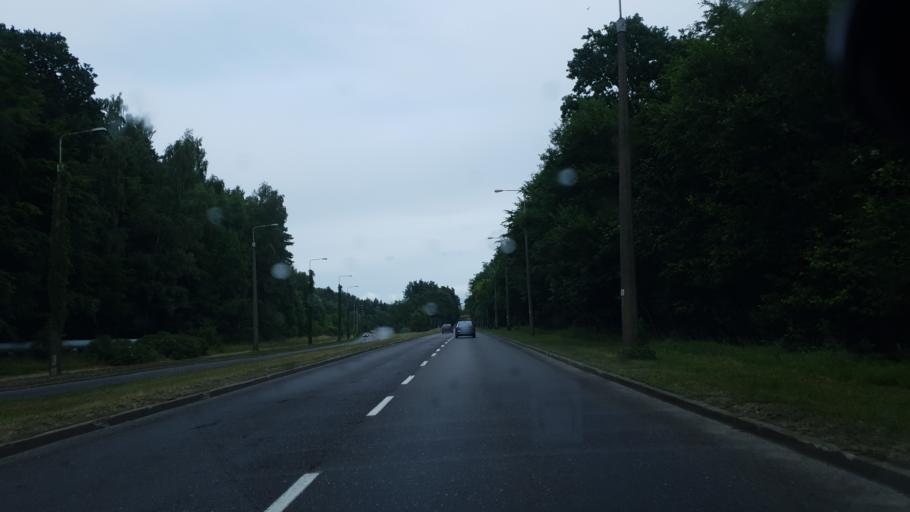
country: PL
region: Pomeranian Voivodeship
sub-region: Gdynia
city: Wielki Kack
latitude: 54.4660
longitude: 18.4678
